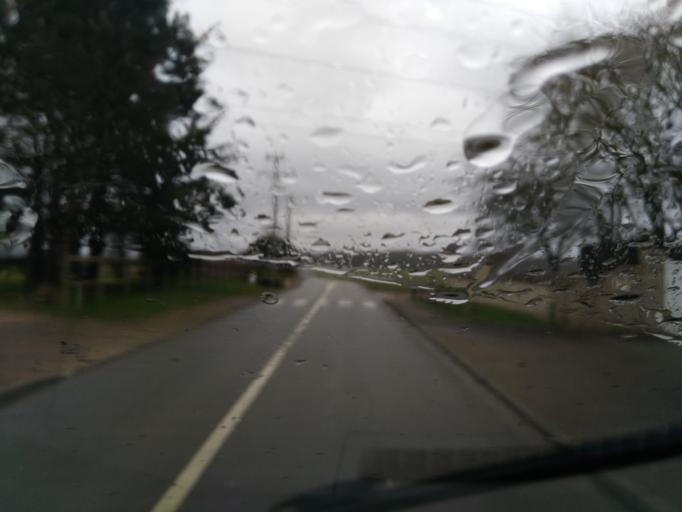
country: FR
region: Ile-de-France
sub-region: Departement des Yvelines
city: Thoiry
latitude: 48.8577
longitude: 1.8289
